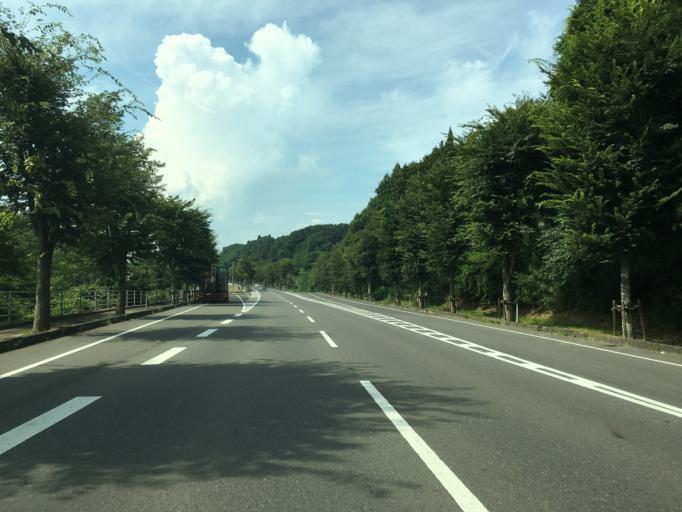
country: JP
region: Fukushima
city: Sukagawa
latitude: 37.2408
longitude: 140.4350
